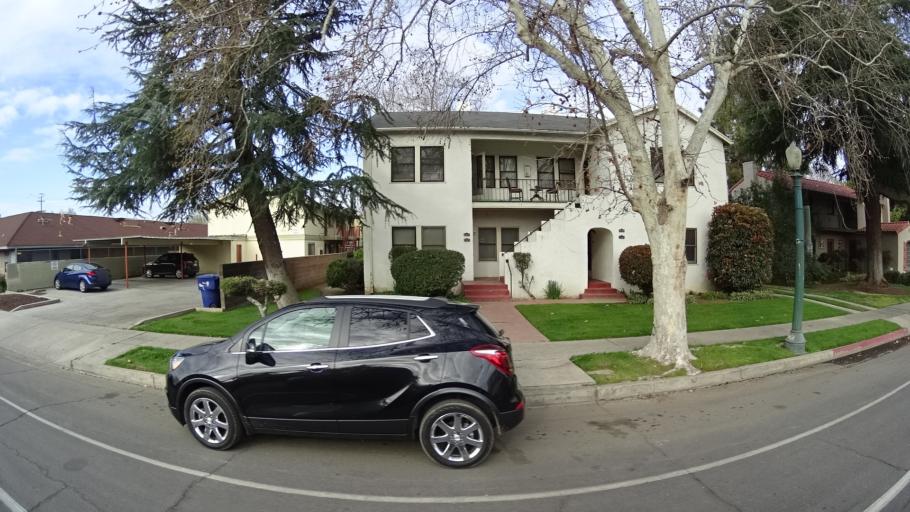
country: US
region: California
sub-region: Fresno County
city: Fresno
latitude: 36.7607
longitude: -119.8011
